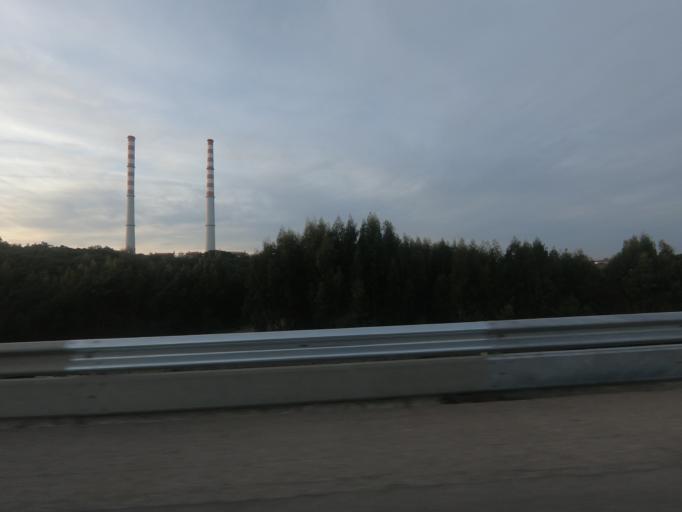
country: PT
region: Setubal
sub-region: Setubal
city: Setubal
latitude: 38.5079
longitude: -8.8388
